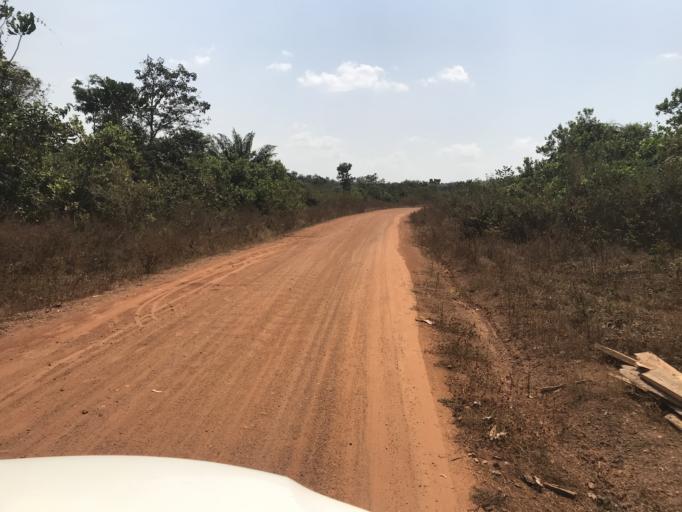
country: NG
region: Osun
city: Ifon
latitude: 7.9012
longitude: 4.4782
